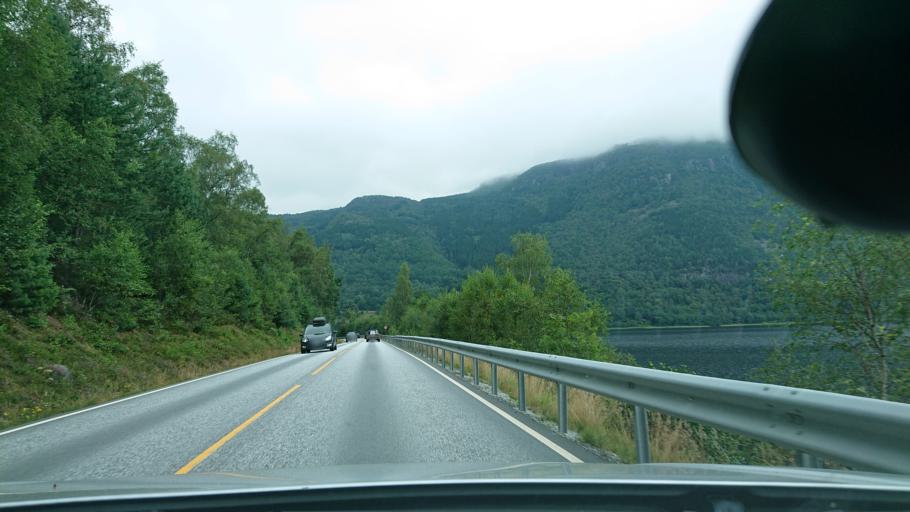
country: NO
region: Rogaland
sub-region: Hjelmeland
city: Hjelmelandsvagen
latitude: 59.1578
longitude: 6.1744
